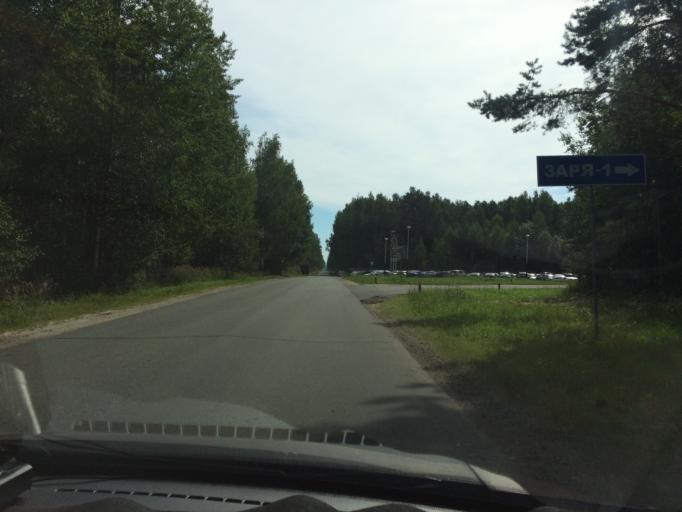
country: RU
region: Mariy-El
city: Surok
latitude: 56.5703
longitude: 48.2275
